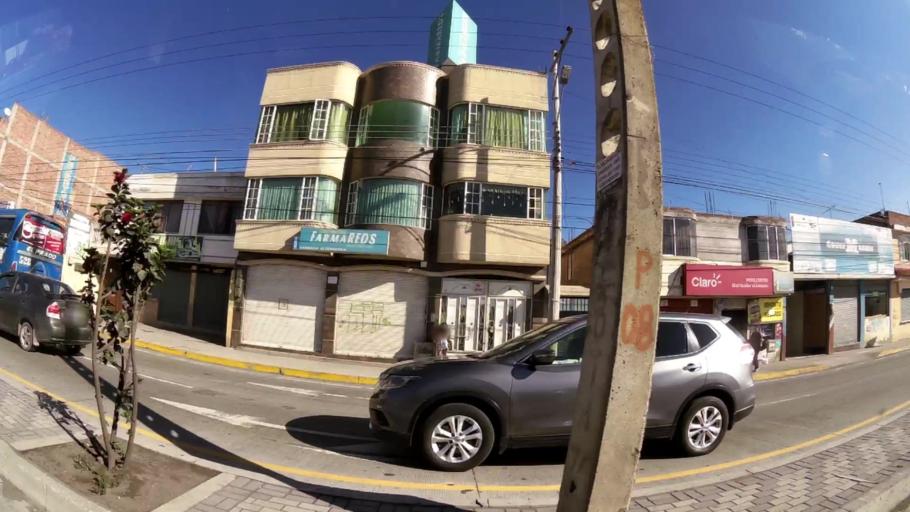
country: EC
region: Chimborazo
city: Riobamba
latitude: -1.6465
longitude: -78.6811
